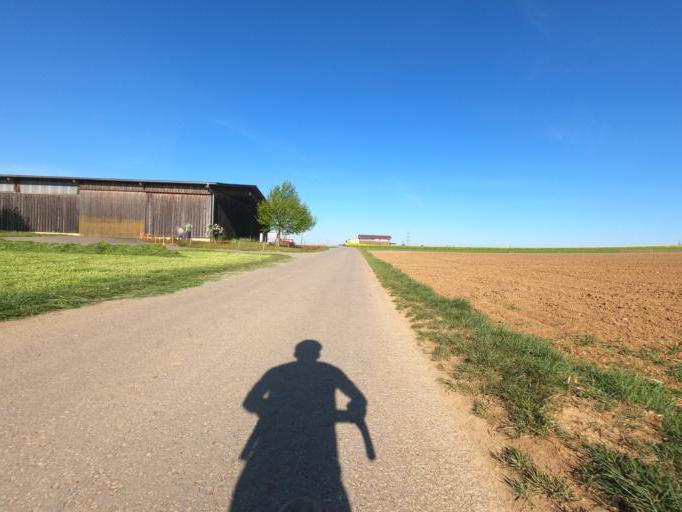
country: DE
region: Baden-Wuerttemberg
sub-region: Regierungsbezirk Stuttgart
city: Aidlingen
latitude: 48.7095
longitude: 8.9268
